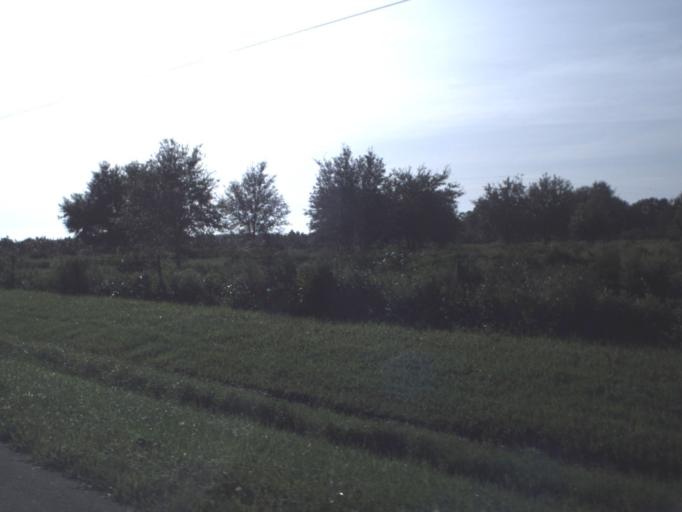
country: US
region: Florida
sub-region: DeSoto County
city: Nocatee
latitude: 27.2016
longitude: -81.9496
